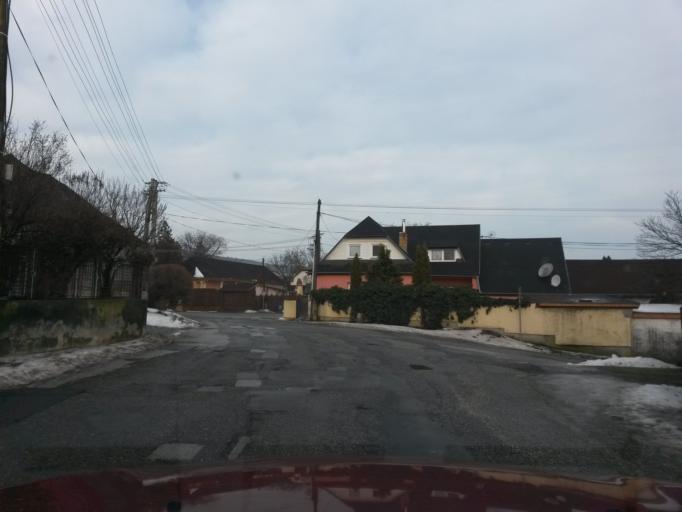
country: SK
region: Kosicky
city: Kosice
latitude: 48.7471
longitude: 21.3223
